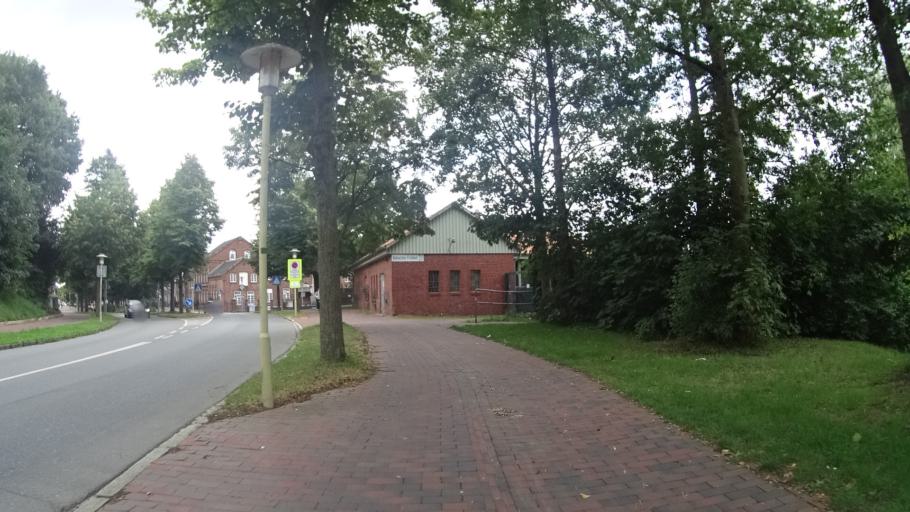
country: DE
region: Schleswig-Holstein
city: Gluckstadt
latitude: 53.7903
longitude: 9.4196
